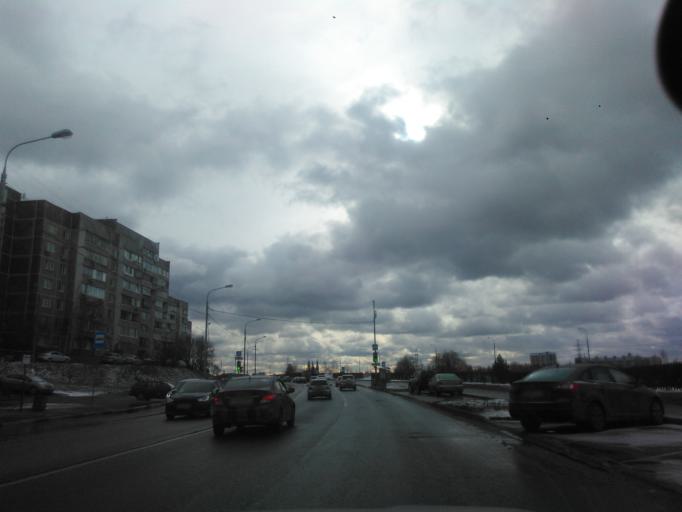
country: RU
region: Moskovskaya
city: Pavshino
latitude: 55.8405
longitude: 37.3577
